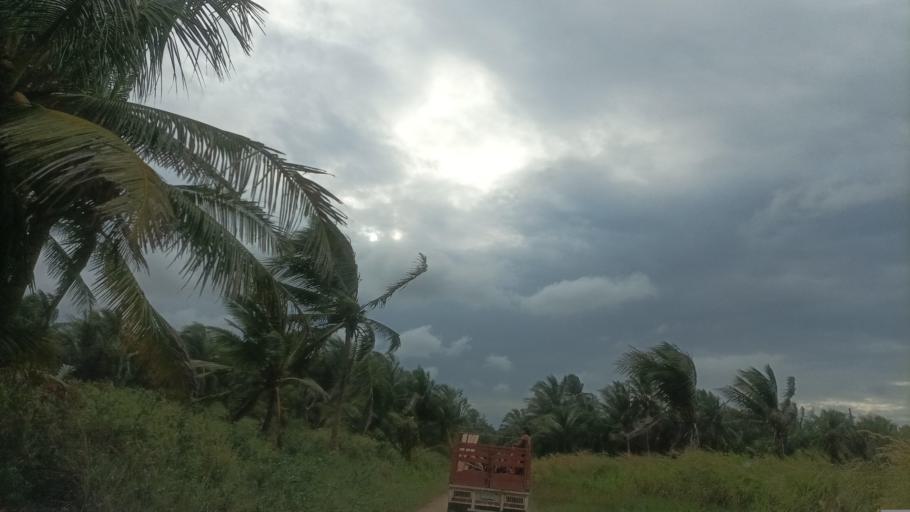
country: MX
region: Veracruz
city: Allende
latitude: 18.1779
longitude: -94.2747
